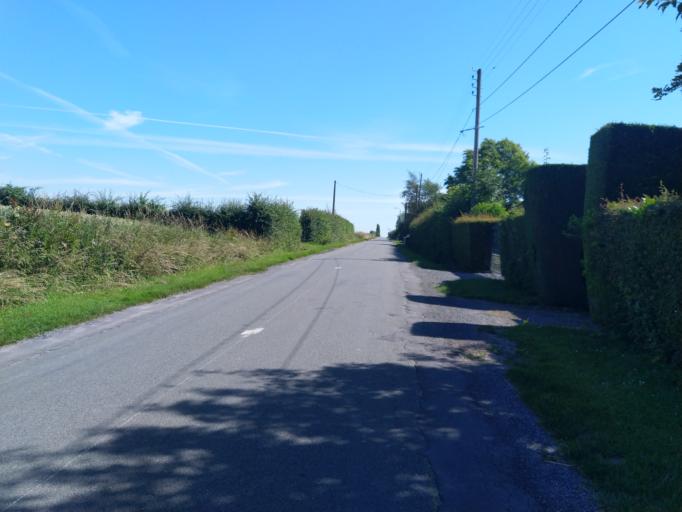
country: FR
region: Nord-Pas-de-Calais
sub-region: Departement du Nord
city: La Longueville
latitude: 50.3341
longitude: 3.8389
